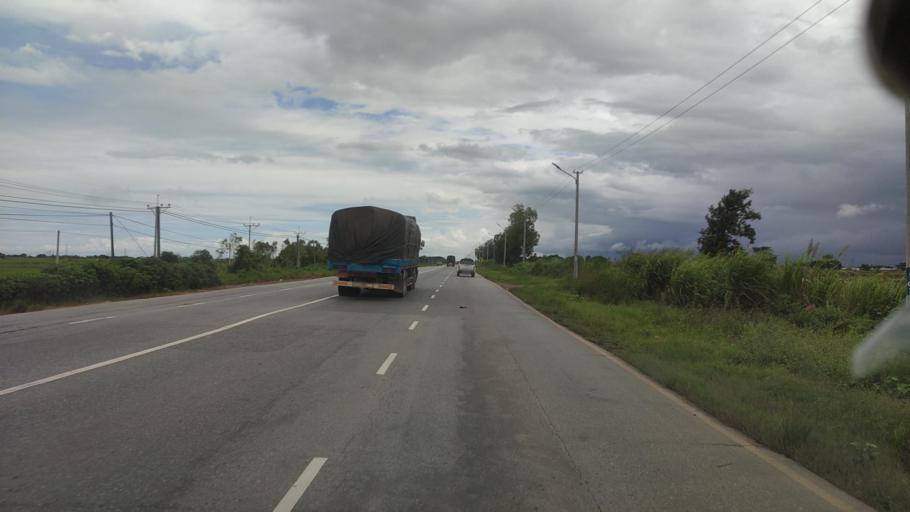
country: MM
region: Bago
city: Bago
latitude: 17.4294
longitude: 96.5249
